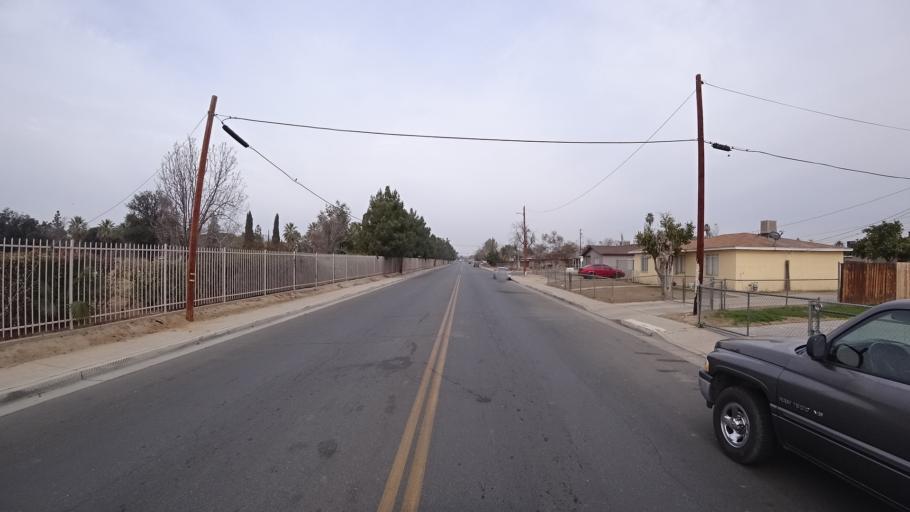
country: US
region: California
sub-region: Kern County
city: Bakersfield
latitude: 35.3616
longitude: -118.9909
